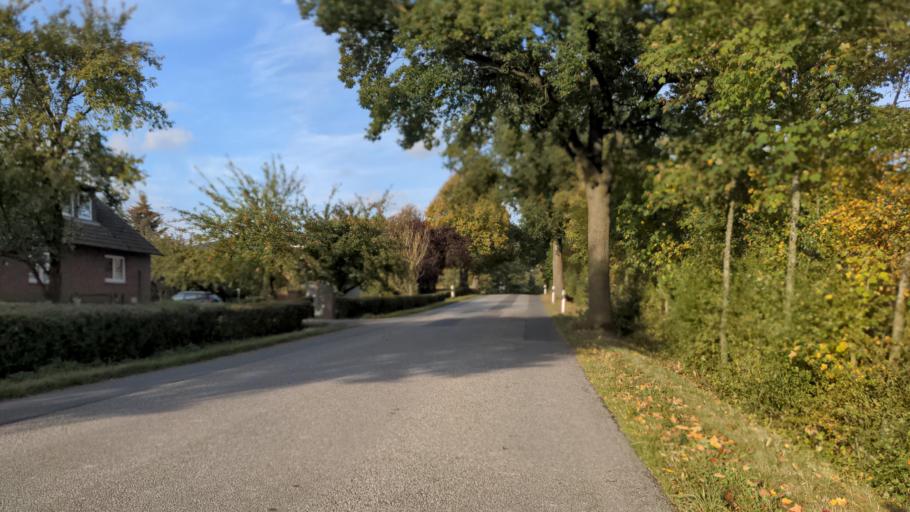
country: DE
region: Schleswig-Holstein
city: Ahrensbok
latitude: 53.9895
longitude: 10.5727
